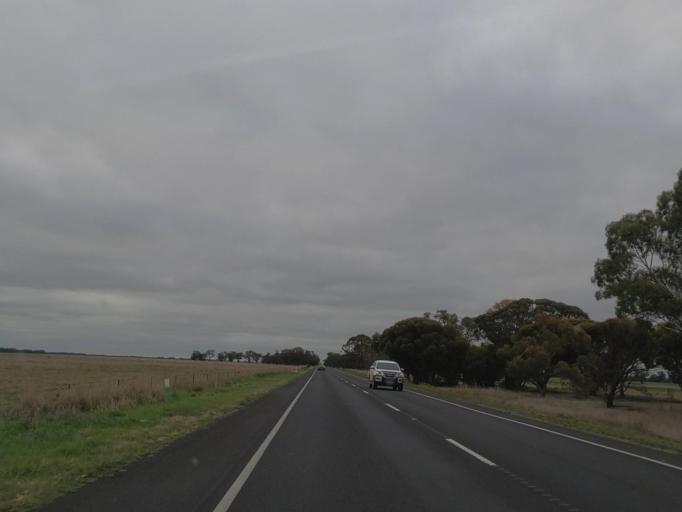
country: AU
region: Victoria
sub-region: Greater Bendigo
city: Long Gully
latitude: -36.2855
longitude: 143.9709
